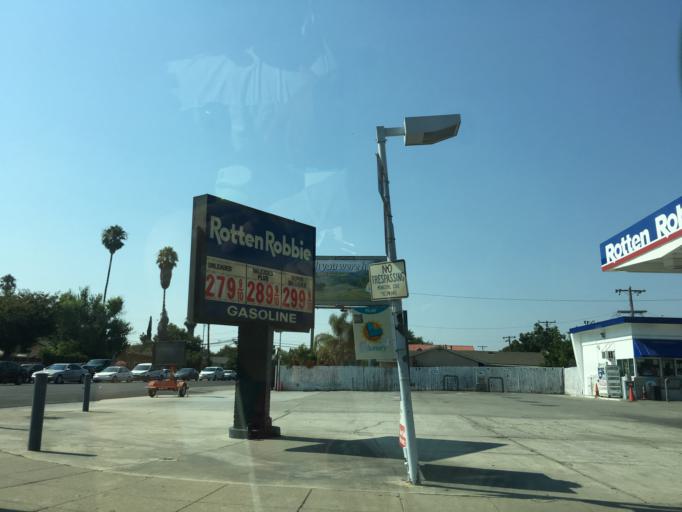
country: US
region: California
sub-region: Santa Clara County
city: Alum Rock
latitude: 37.3473
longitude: -121.8324
